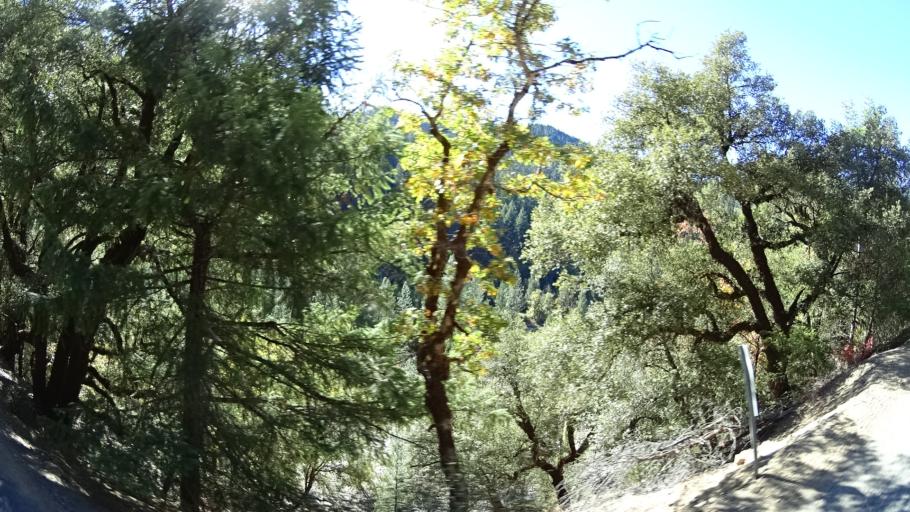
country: US
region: California
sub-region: Siskiyou County
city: Happy Camp
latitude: 41.3037
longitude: -123.1619
